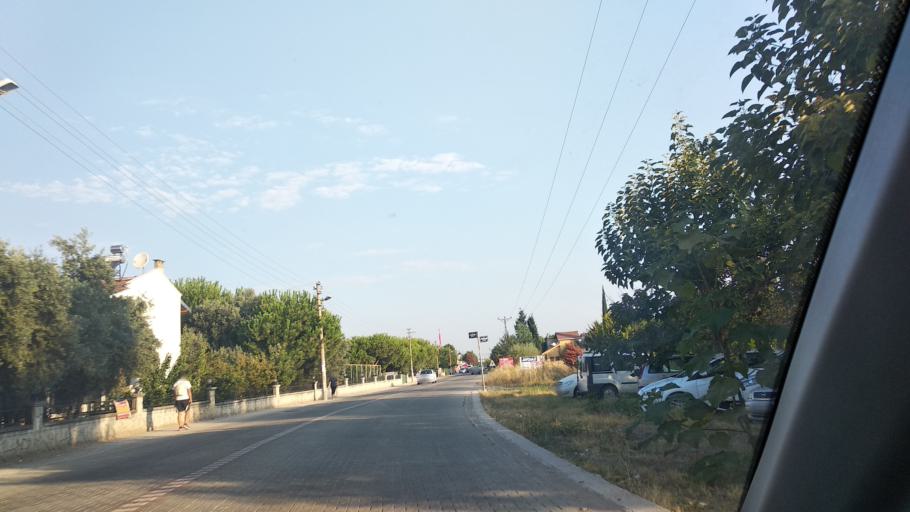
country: TR
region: Balikesir
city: Altinova
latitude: 39.1562
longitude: 26.8245
